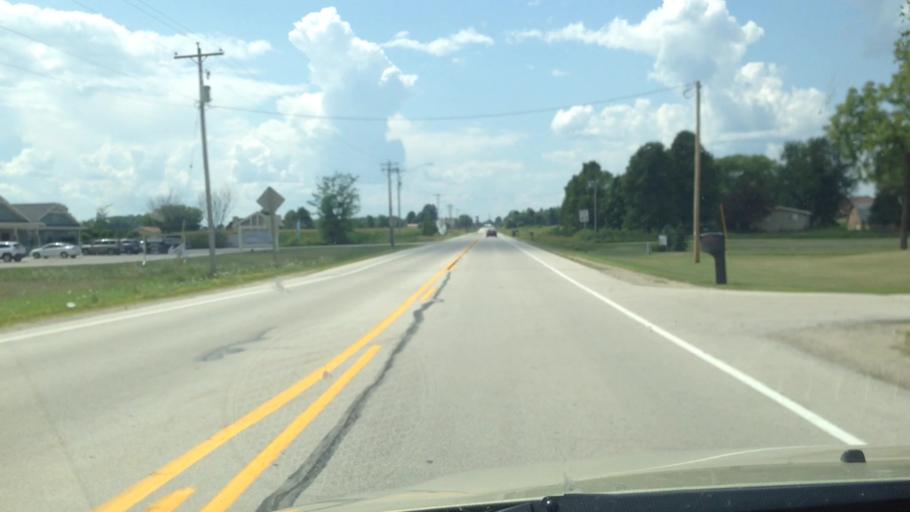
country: US
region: Wisconsin
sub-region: Brown County
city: Pulaski
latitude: 44.6571
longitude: -88.2238
